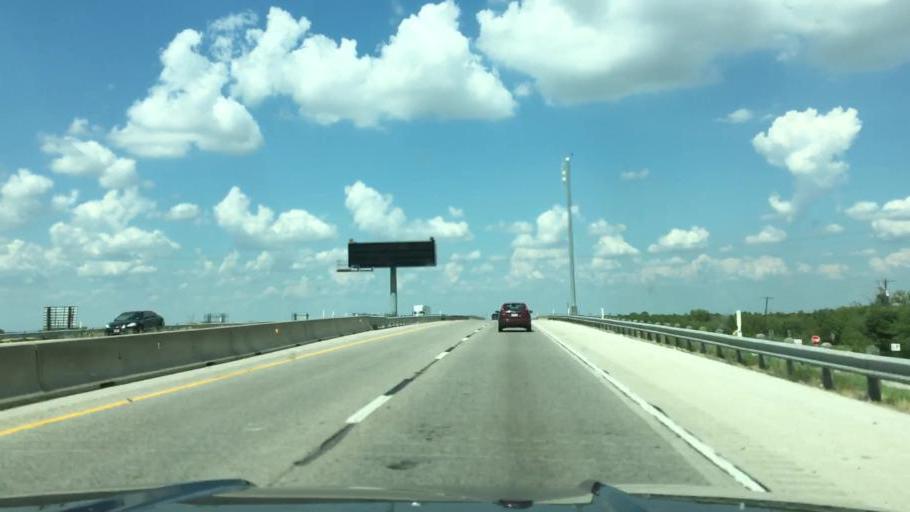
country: US
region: Texas
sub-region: Tarrant County
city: Haslet
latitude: 32.9409
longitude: -97.3129
